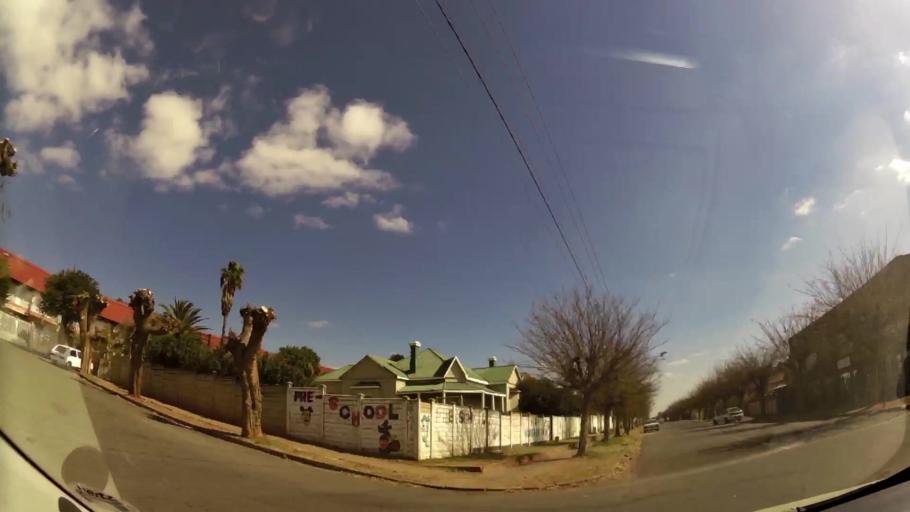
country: ZA
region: Gauteng
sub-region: West Rand District Municipality
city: Krugersdorp
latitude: -26.1085
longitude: 27.7815
